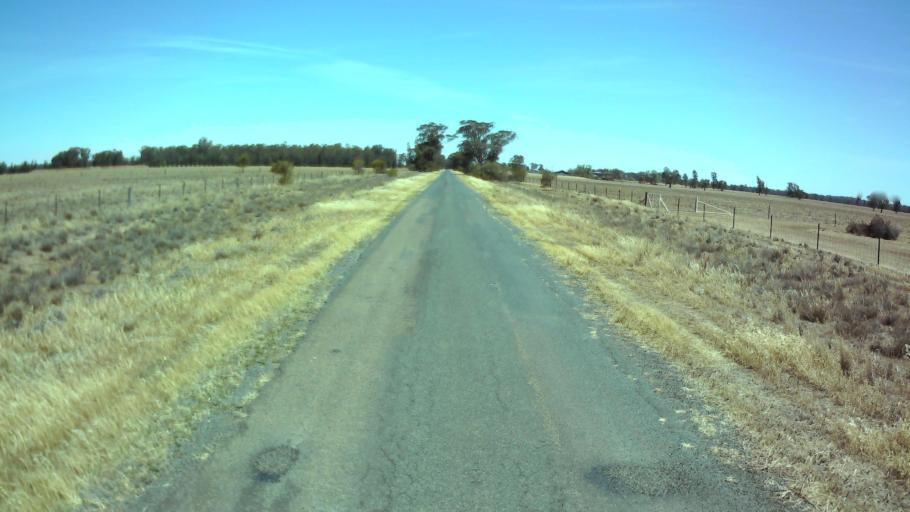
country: AU
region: New South Wales
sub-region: Weddin
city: Grenfell
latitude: -33.8982
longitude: 147.6869
